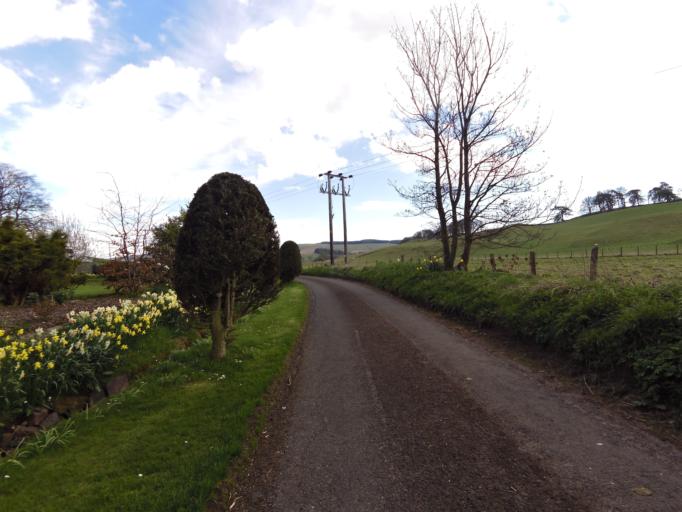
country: GB
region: Scotland
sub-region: Fife
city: Newburgh
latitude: 56.3349
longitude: -3.2421
